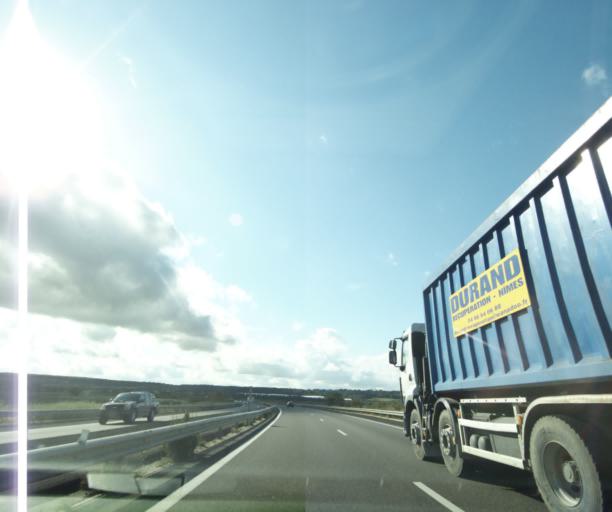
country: FR
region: Languedoc-Roussillon
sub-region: Departement du Gard
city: Bellegarde
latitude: 43.7283
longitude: 4.4994
